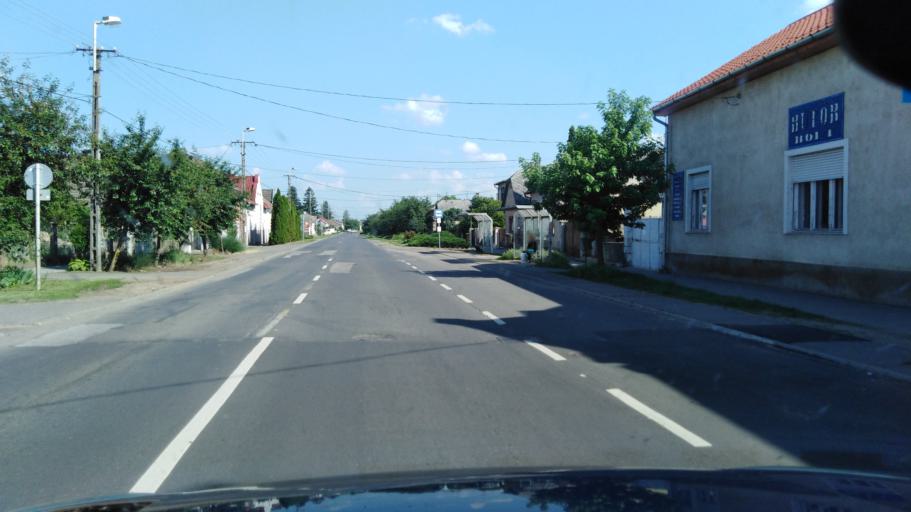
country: HU
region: Szabolcs-Szatmar-Bereg
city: Nyirbator
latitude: 47.8330
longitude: 22.1350
